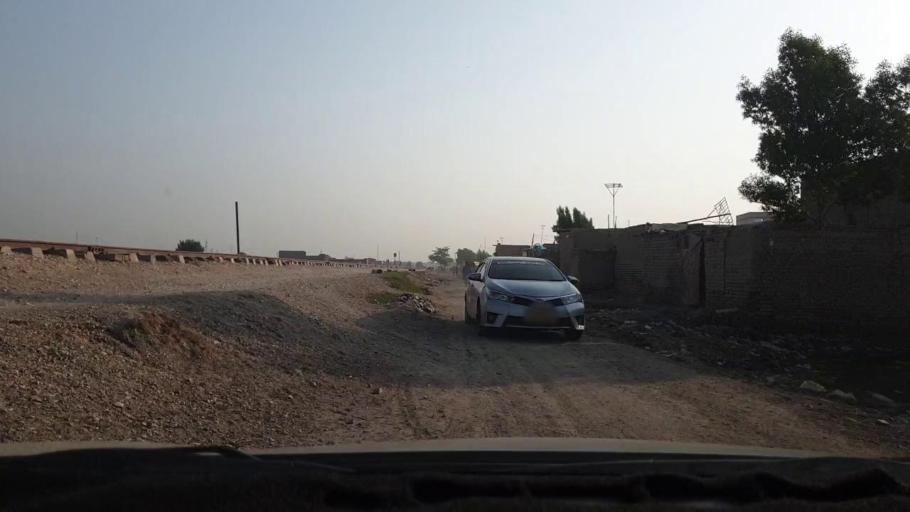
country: PK
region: Sindh
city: Larkana
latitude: 27.5311
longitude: 68.2003
